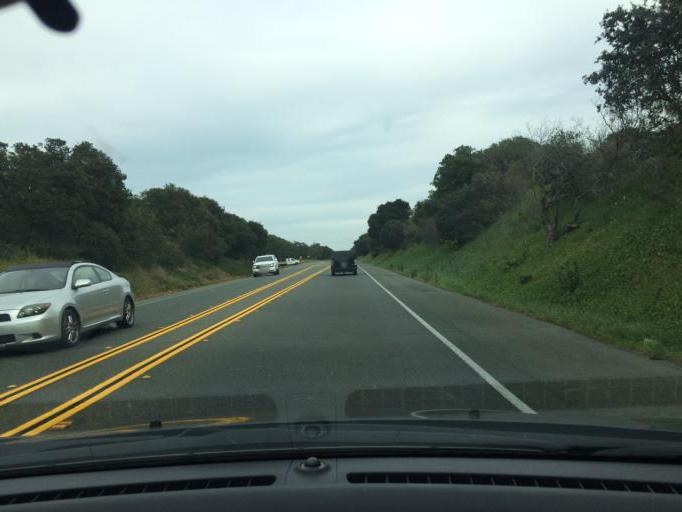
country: US
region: California
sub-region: Monterey County
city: Prunedale
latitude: 36.7793
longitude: -121.7057
